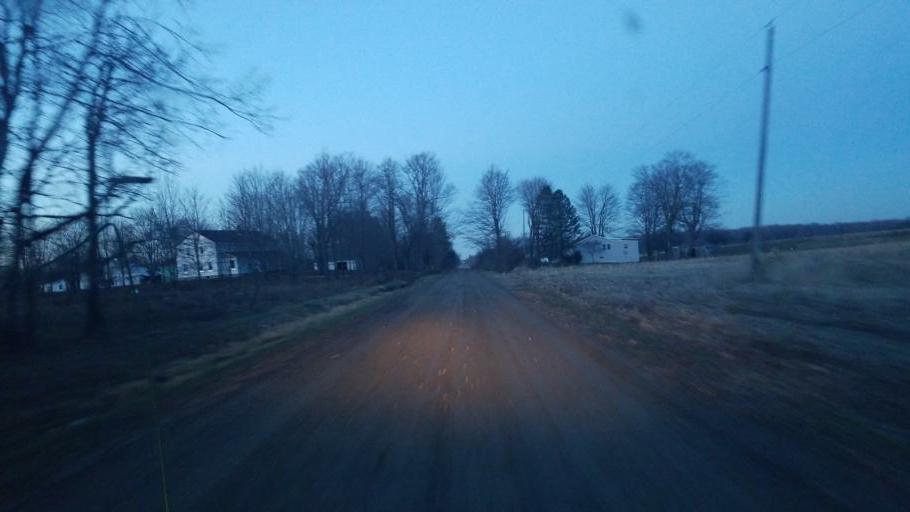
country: US
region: Ohio
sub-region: Ashtabula County
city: Andover
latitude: 41.6275
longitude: -80.6782
